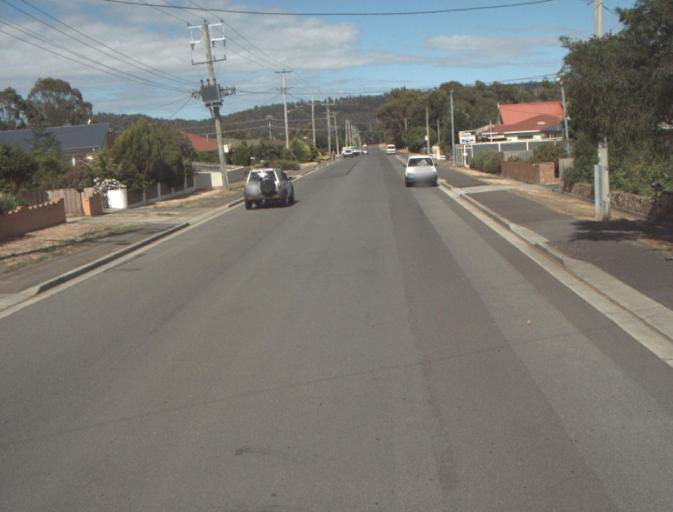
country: AU
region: Tasmania
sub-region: Launceston
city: Summerhill
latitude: -41.4701
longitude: 147.1224
